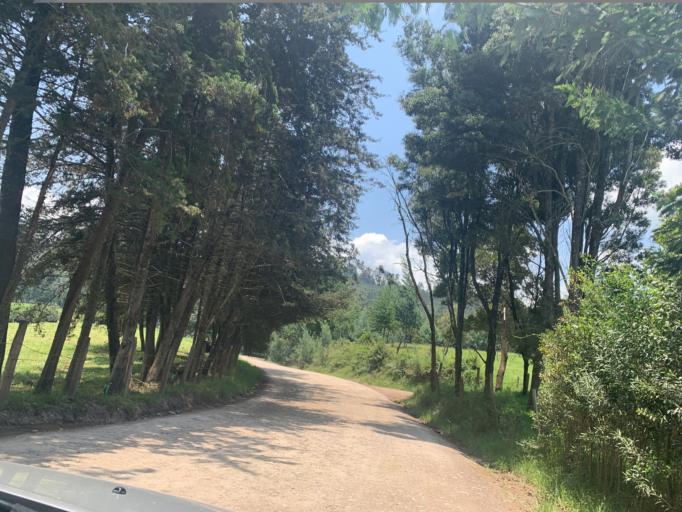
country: CO
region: Boyaca
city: Chiquinquira
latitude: 5.5842
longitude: -73.7472
